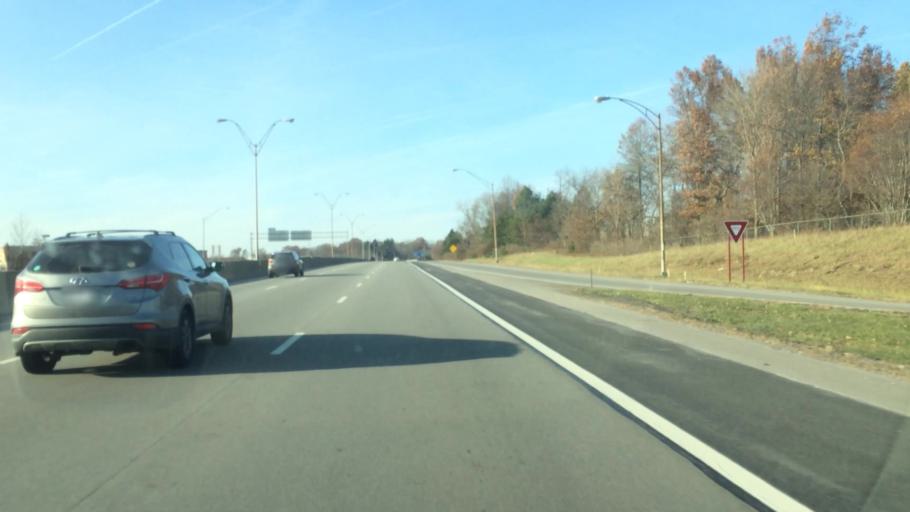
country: US
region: Ohio
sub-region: Summit County
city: Silver Lake
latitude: 41.1643
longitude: -81.4729
